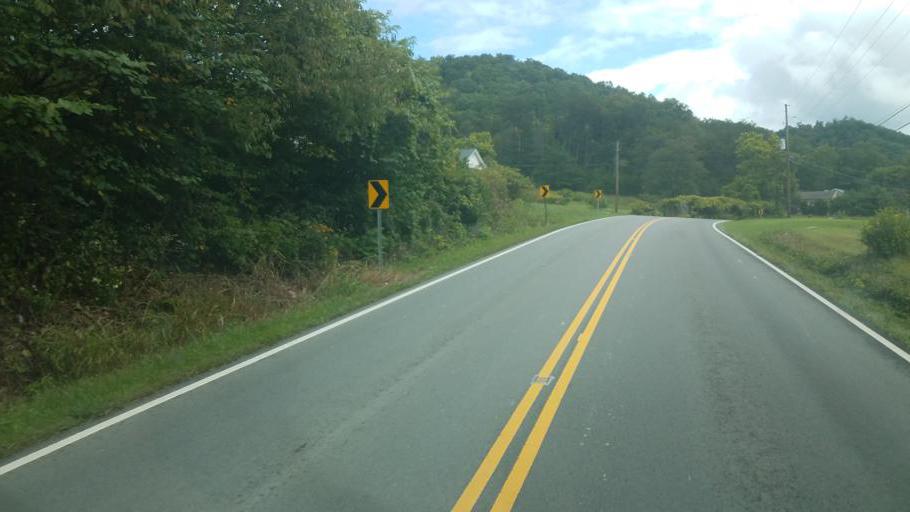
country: US
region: Ohio
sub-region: Scioto County
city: Lucasville
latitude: 38.8705
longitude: -82.9454
